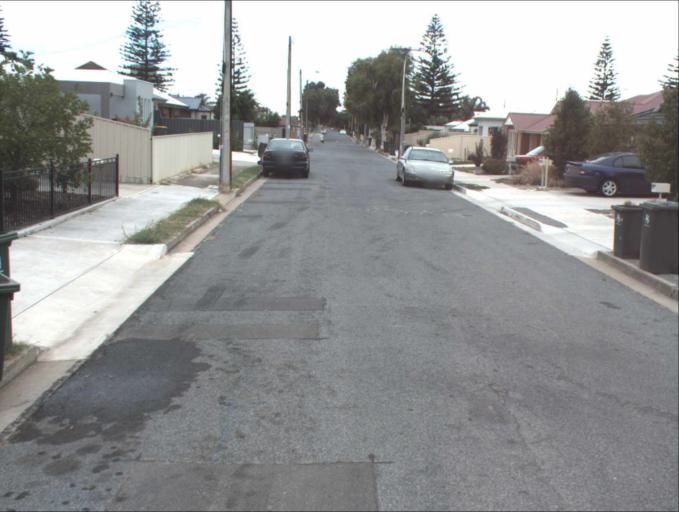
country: AU
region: South Australia
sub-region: Port Adelaide Enfield
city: Birkenhead
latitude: -34.8025
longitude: 138.4978
